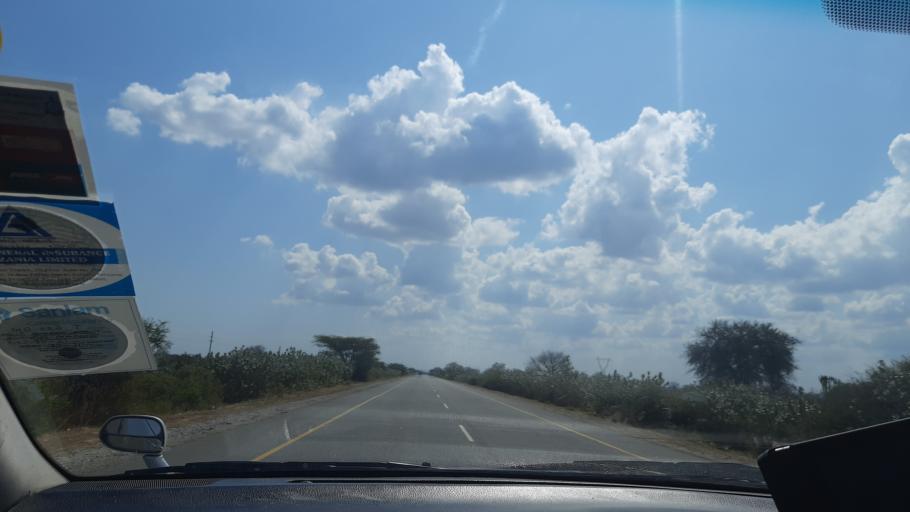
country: TZ
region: Singida
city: Kintinku
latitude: -5.9301
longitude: 35.2765
